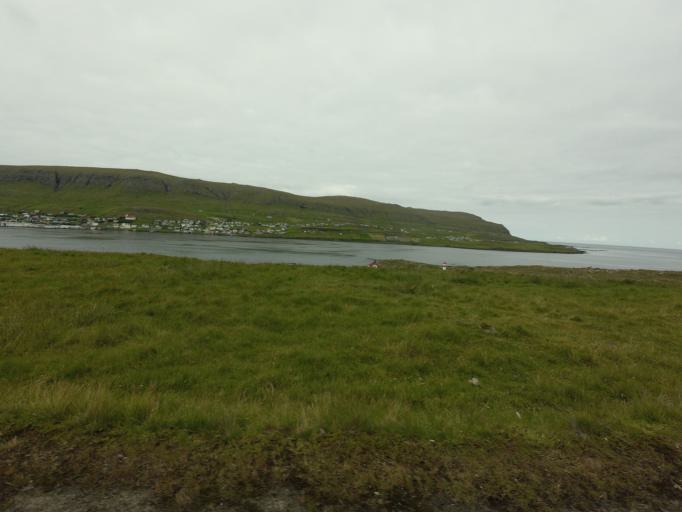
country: FO
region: Suduroy
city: Tvoroyri
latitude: 61.5422
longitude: -6.8067
